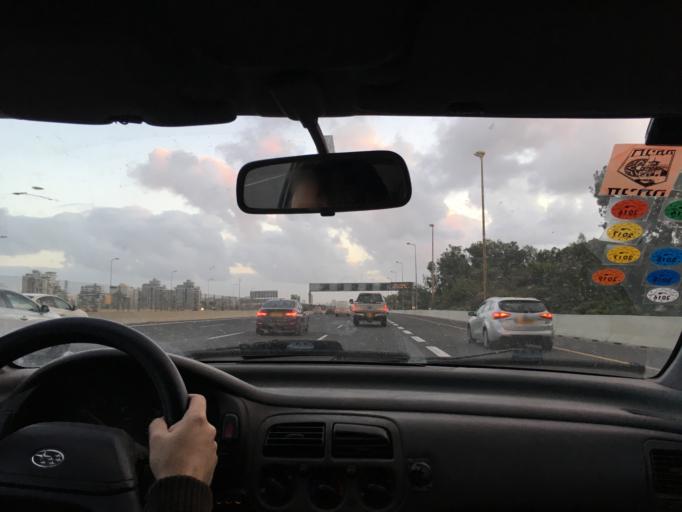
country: IL
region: Tel Aviv
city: Ramat HaSharon
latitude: 32.1326
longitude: 34.8096
